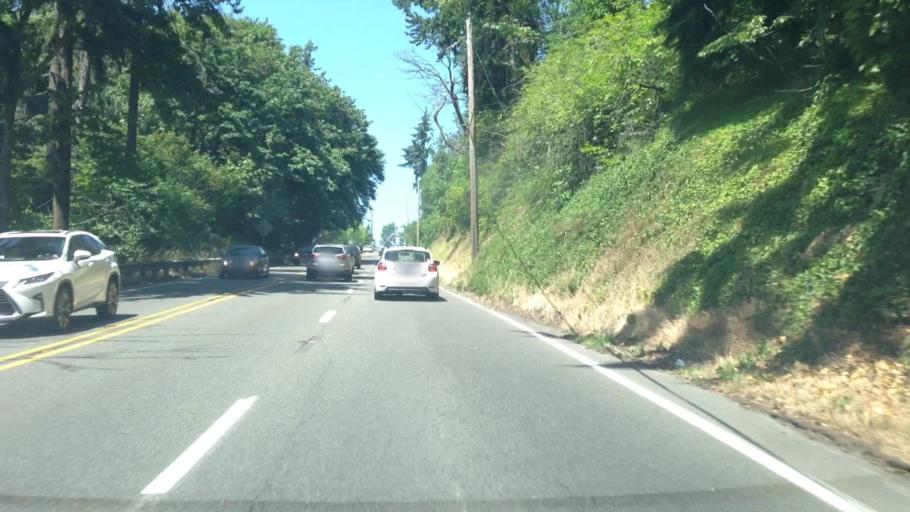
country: US
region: Washington
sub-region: Pierce County
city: North Puyallup
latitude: 47.2220
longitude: -122.2934
